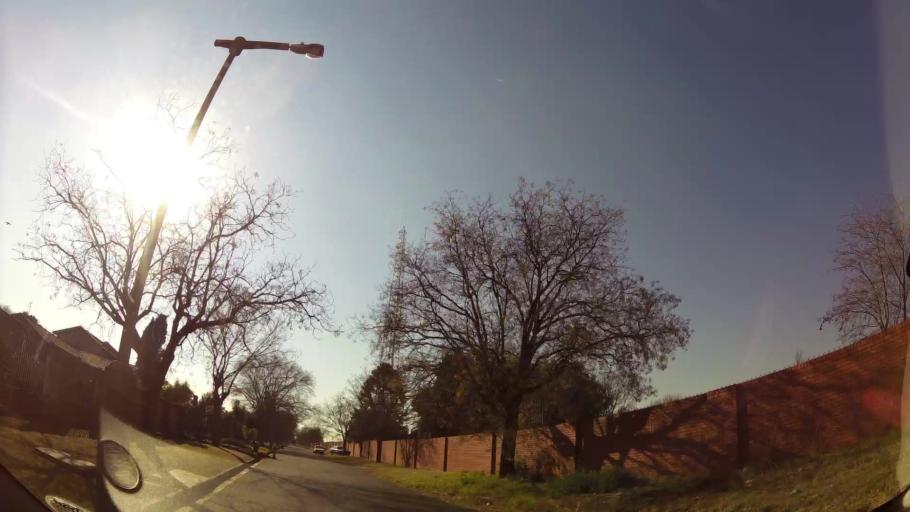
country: ZA
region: Gauteng
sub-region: Ekurhuleni Metropolitan Municipality
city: Benoni
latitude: -26.1580
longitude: 28.3056
